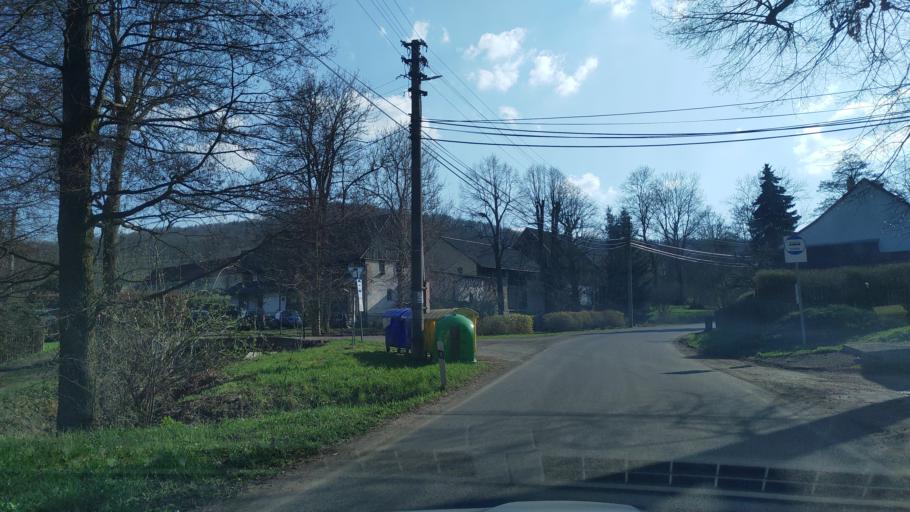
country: CZ
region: Ustecky
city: Vernerice
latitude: 50.6848
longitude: 14.3398
